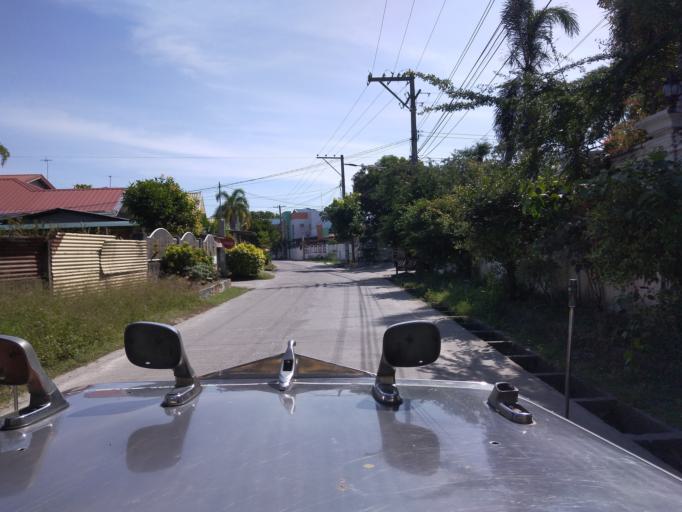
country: PH
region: Central Luzon
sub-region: Province of Pampanga
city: Bacolor
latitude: 15.0050
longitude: 120.6694
